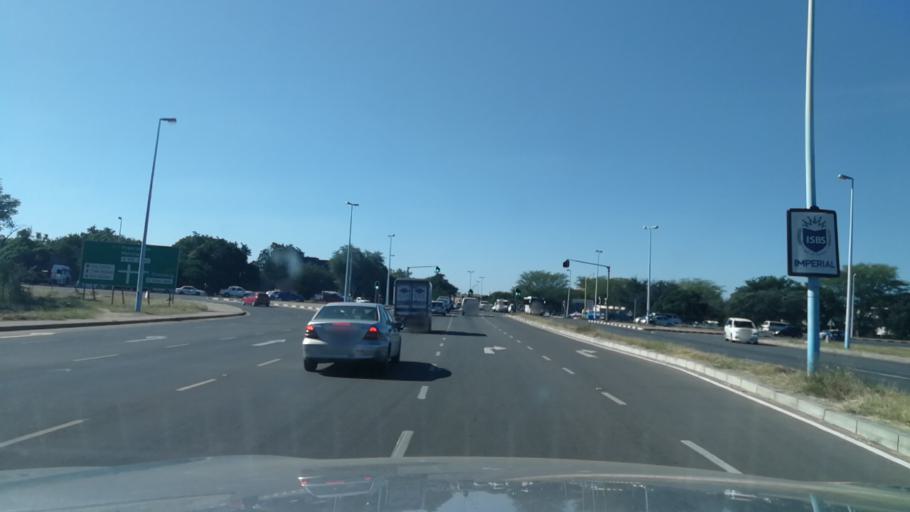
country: BW
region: South East
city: Gaborone
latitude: -24.6734
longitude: 25.9236
